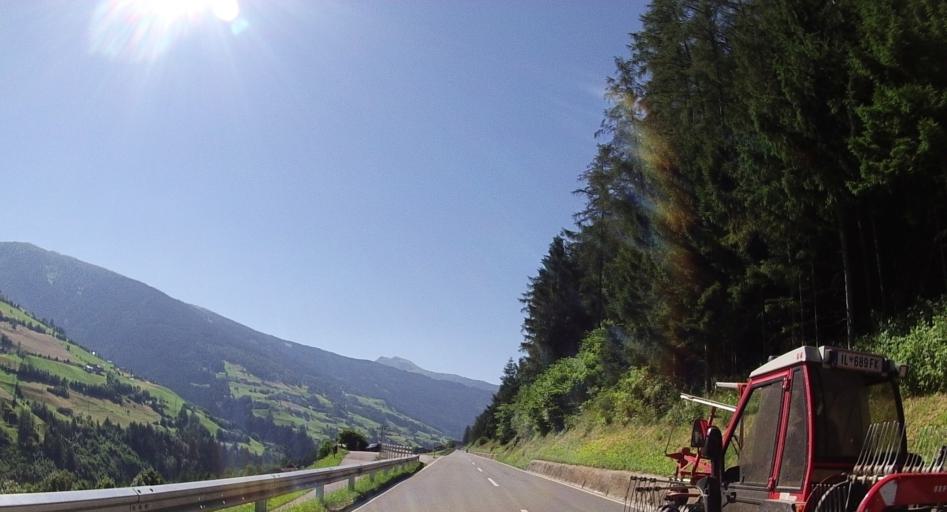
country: AT
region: Tyrol
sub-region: Politischer Bezirk Innsbruck Land
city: Schoenberg im Stubaital
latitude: 47.1709
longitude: 11.4292
